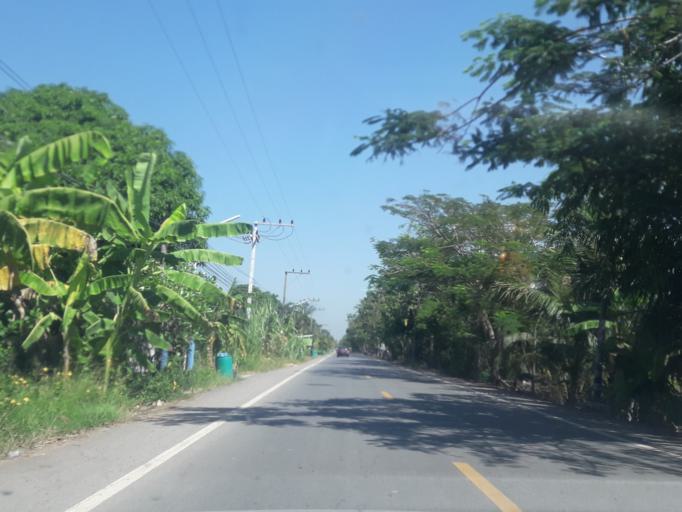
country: TH
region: Pathum Thani
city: Nong Suea
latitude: 14.1734
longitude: 100.8458
